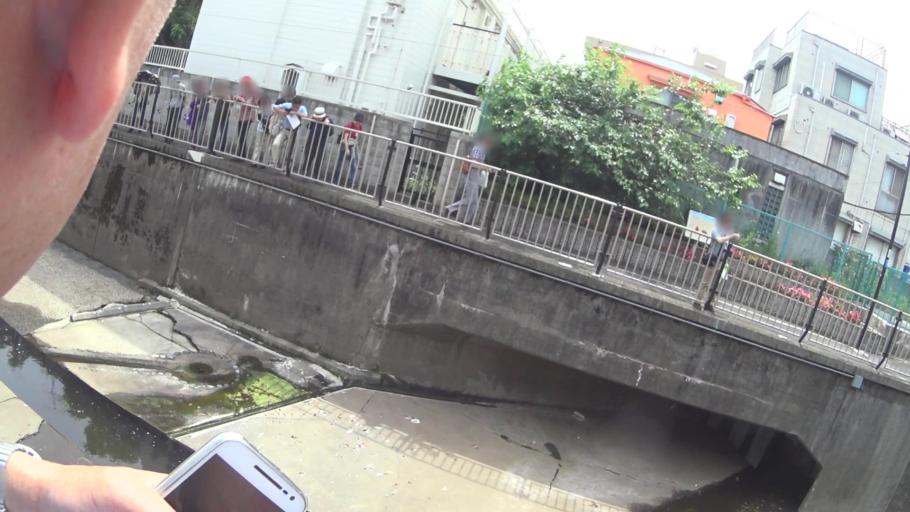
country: JP
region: Tokyo
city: Musashino
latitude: 35.7100
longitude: 139.5976
